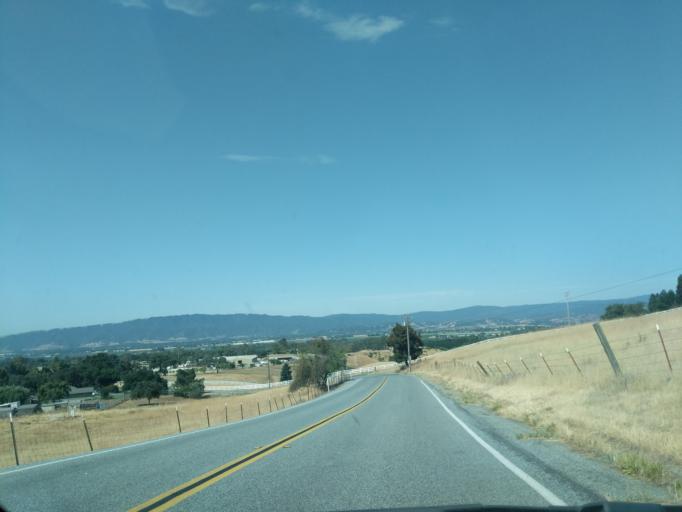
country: US
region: California
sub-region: Santa Clara County
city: Gilroy
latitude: 37.0539
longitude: -121.5262
